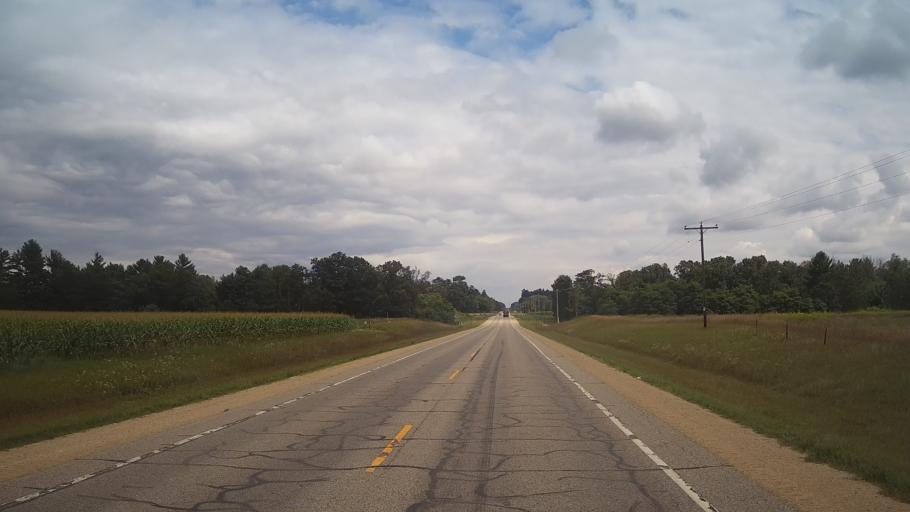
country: US
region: Wisconsin
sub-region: Waushara County
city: Wautoma
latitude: 44.0684
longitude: -89.3422
